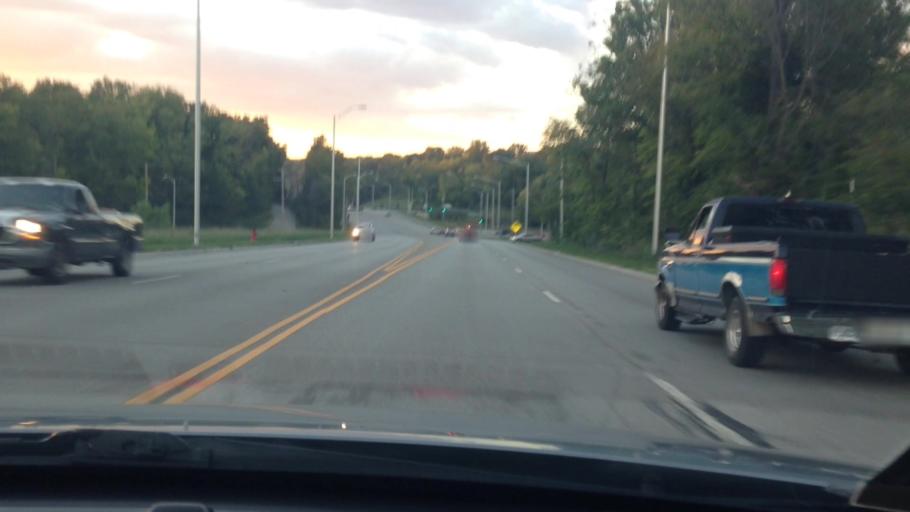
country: US
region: Missouri
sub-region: Jackson County
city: Raytown
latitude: 39.0277
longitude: -94.5071
